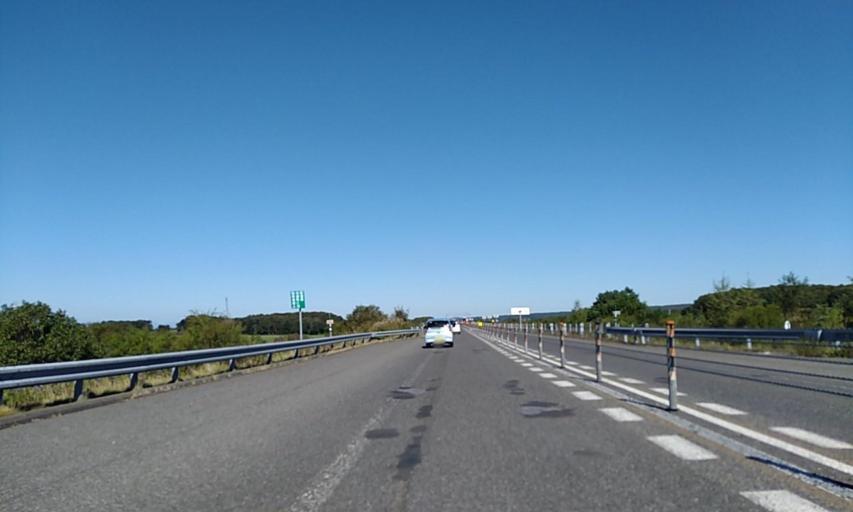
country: JP
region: Hokkaido
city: Tomakomai
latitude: 42.5569
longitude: 141.9868
